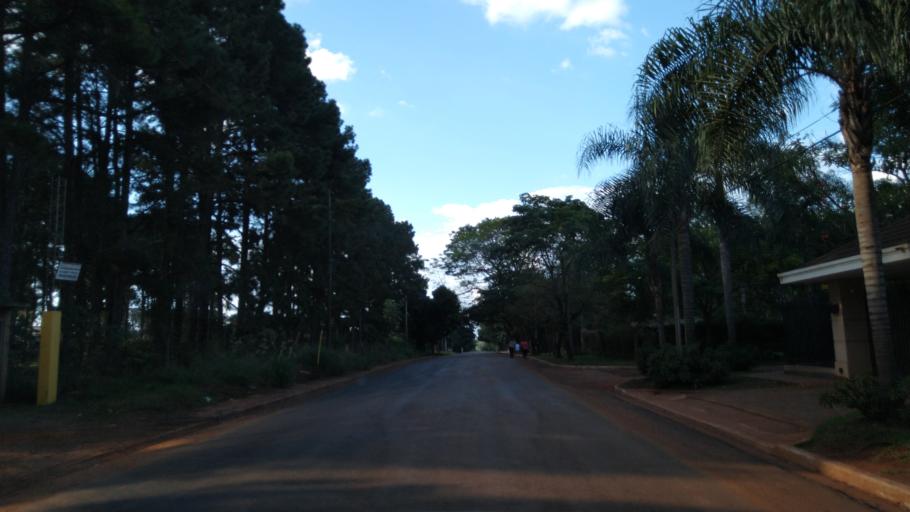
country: AR
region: Misiones
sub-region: Departamento de Capital
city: Posadas
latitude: -27.4045
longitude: -55.9286
